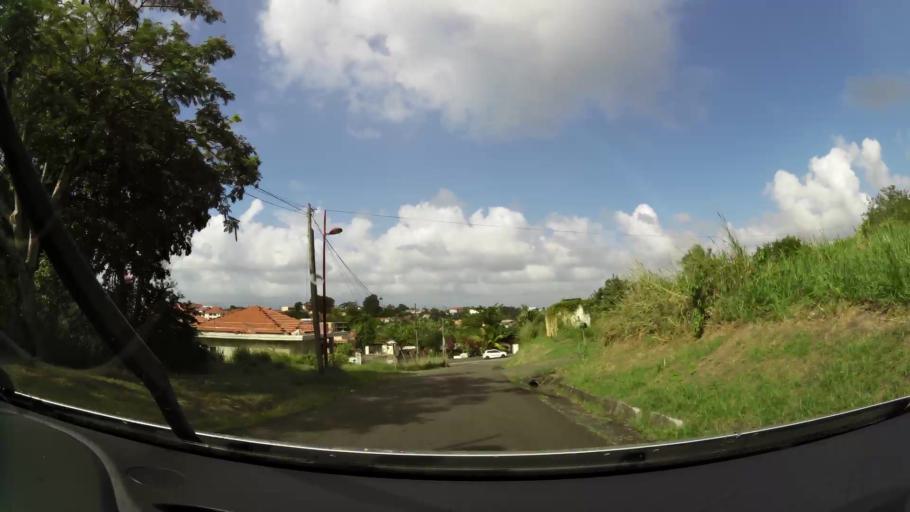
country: MQ
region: Martinique
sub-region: Martinique
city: Les Trois-Ilets
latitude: 14.5356
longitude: -61.0318
